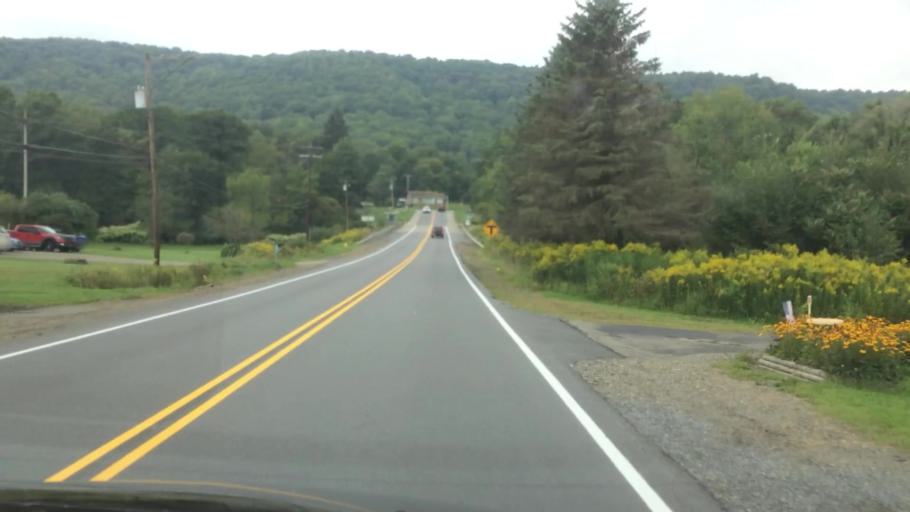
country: US
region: Pennsylvania
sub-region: McKean County
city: Bradford
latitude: 41.9142
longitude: -78.6478
